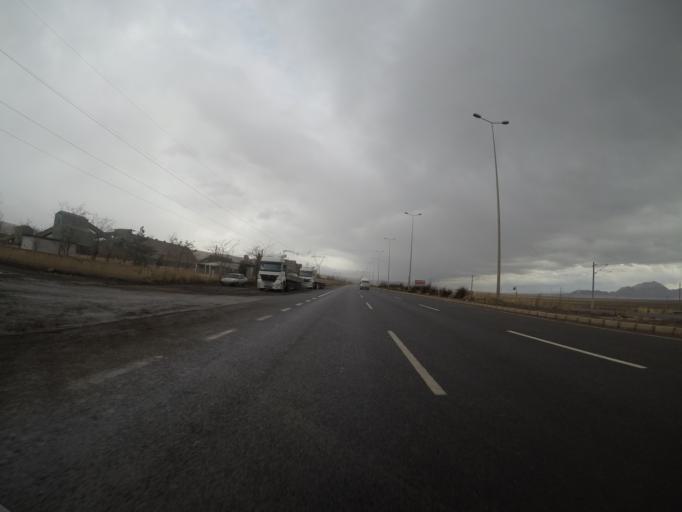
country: TR
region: Kayseri
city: Incesu
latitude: 38.7084
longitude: 35.2601
